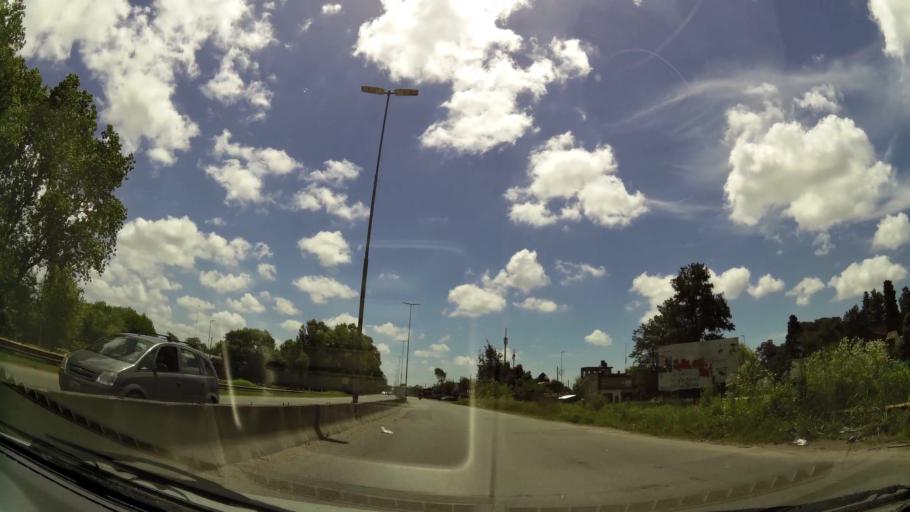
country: AR
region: Buenos Aires
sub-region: Partido de Quilmes
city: Quilmes
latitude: -34.8165
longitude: -58.2267
